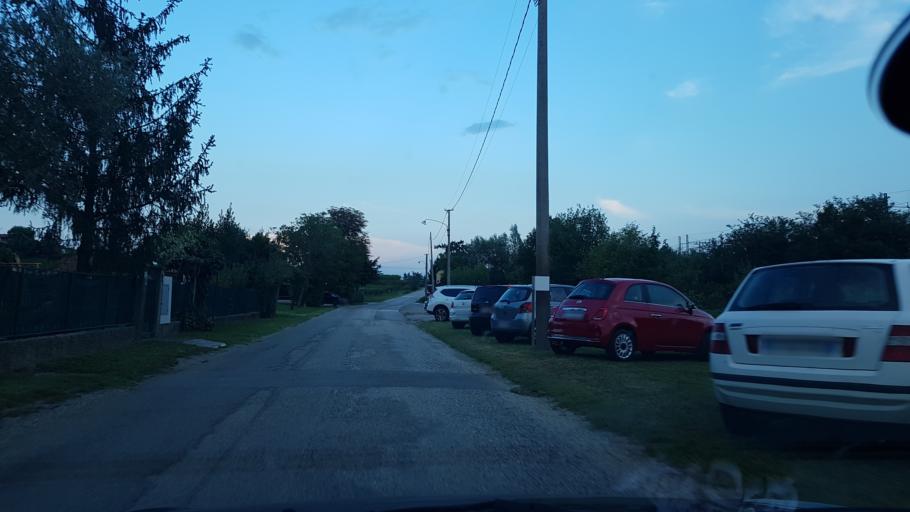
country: IT
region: Friuli Venezia Giulia
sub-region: Provincia di Gorizia
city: Cormons
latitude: 45.9496
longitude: 13.4787
